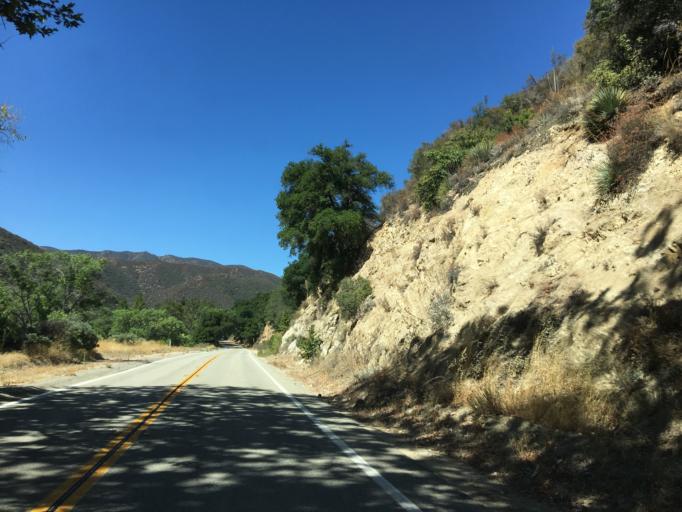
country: US
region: California
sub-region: Los Angeles County
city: Green Valley
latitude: 34.6247
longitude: -118.5521
